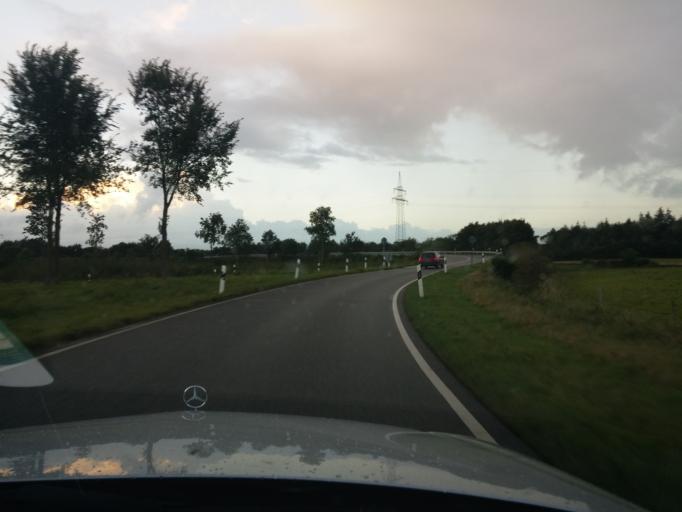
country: DE
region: Schleswig-Holstein
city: Horstedt
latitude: 54.5154
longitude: 9.0676
